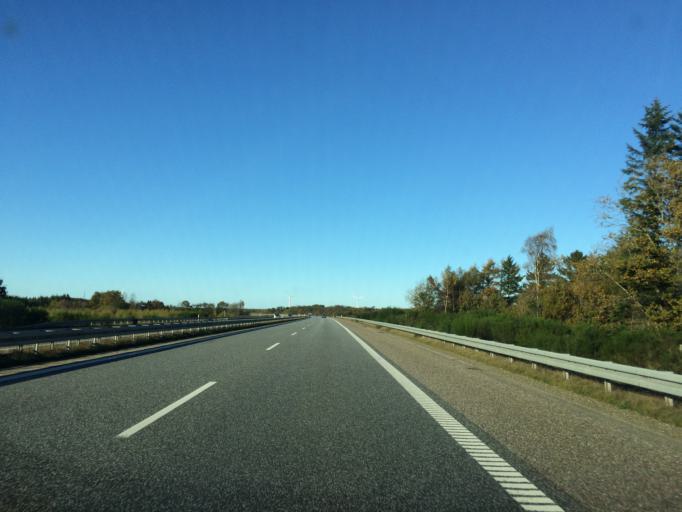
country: DK
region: South Denmark
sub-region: Vejle Kommune
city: Give
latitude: 55.8916
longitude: 9.2179
